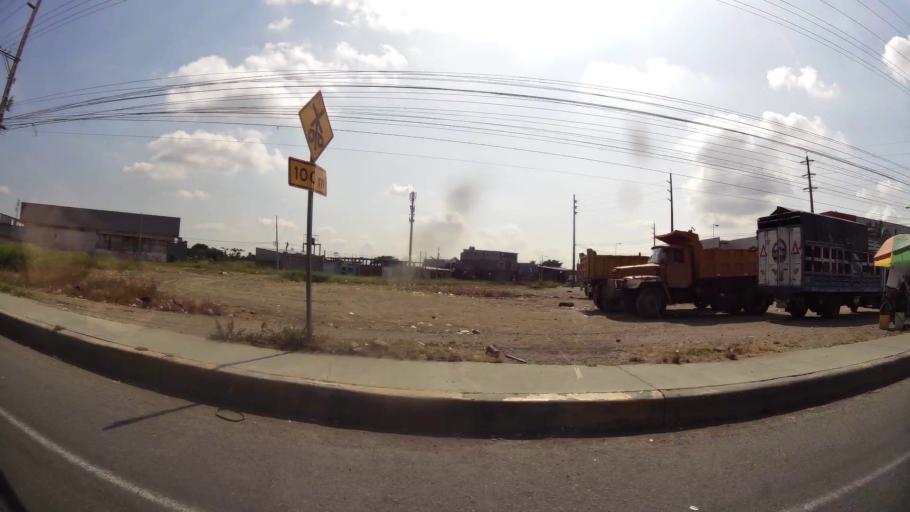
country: EC
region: Guayas
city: Eloy Alfaro
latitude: -2.1771
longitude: -79.8274
